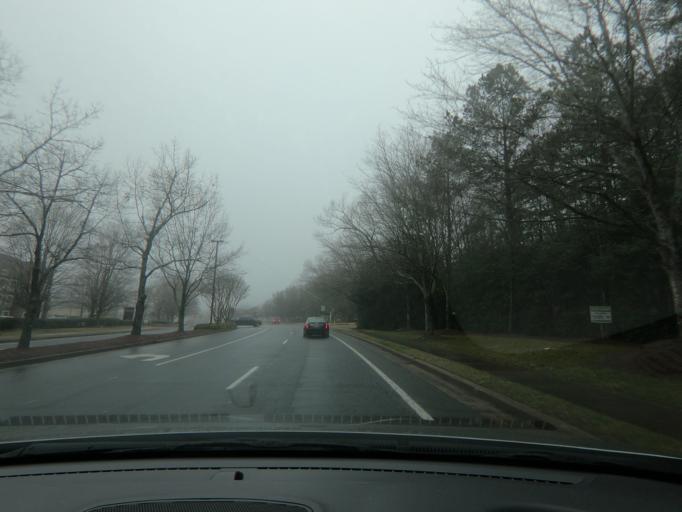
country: US
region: Georgia
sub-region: Fulton County
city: Alpharetta
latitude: 34.0695
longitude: -84.2601
